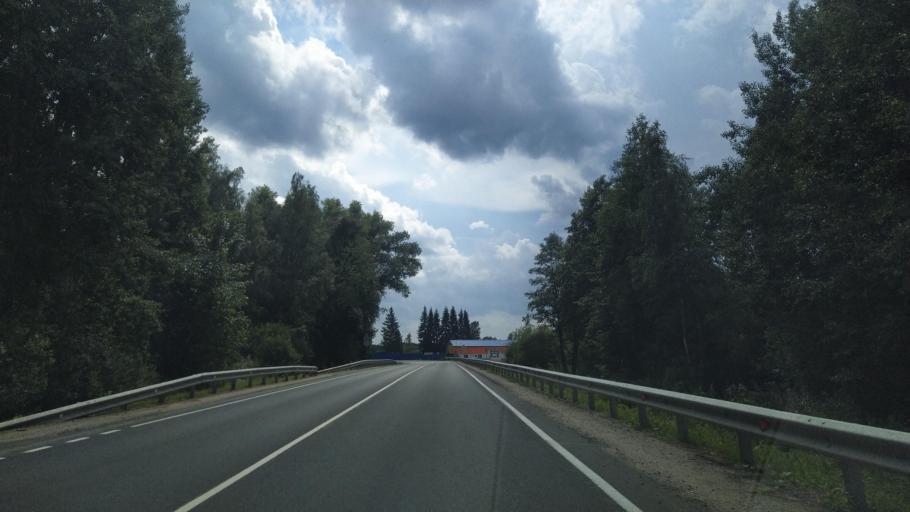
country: RU
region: Pskov
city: Pskov
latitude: 57.7636
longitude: 28.7556
